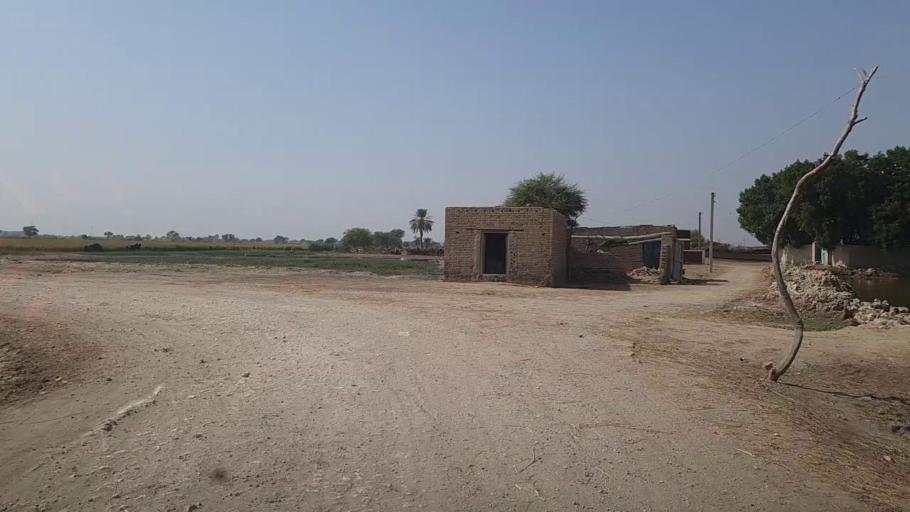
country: PK
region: Sindh
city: Kandhkot
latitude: 28.3959
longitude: 69.2940
